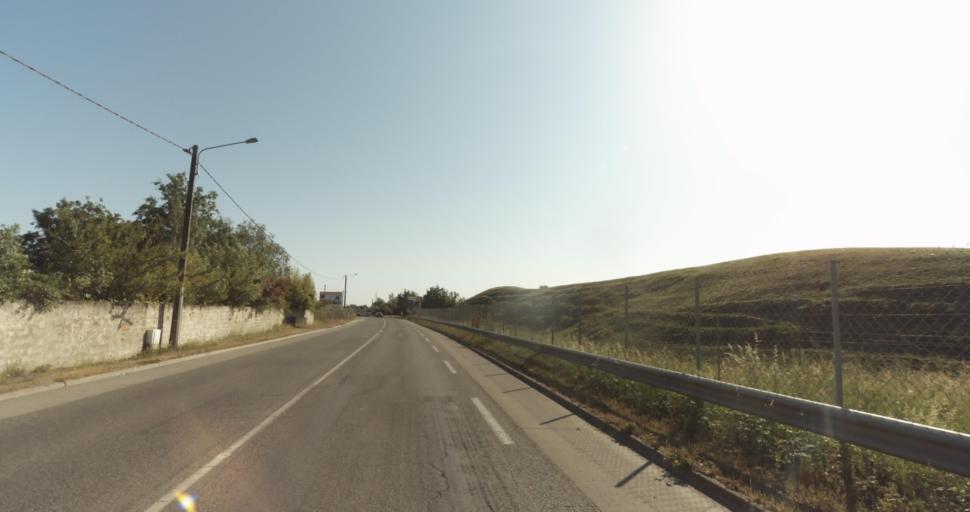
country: FR
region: Midi-Pyrenees
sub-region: Departement de la Haute-Garonne
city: La Salvetat-Saint-Gilles
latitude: 43.5608
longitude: 1.2632
